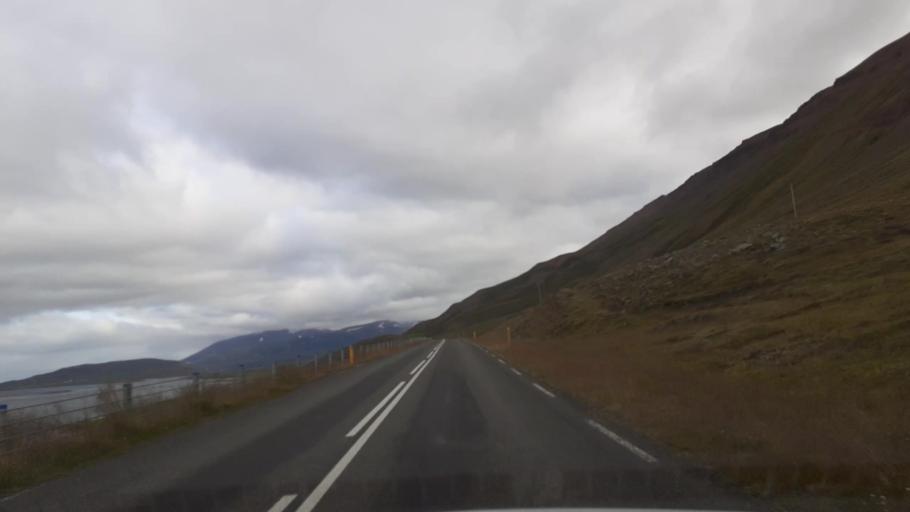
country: IS
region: Northeast
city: Akureyri
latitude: 65.8500
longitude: -18.0603
